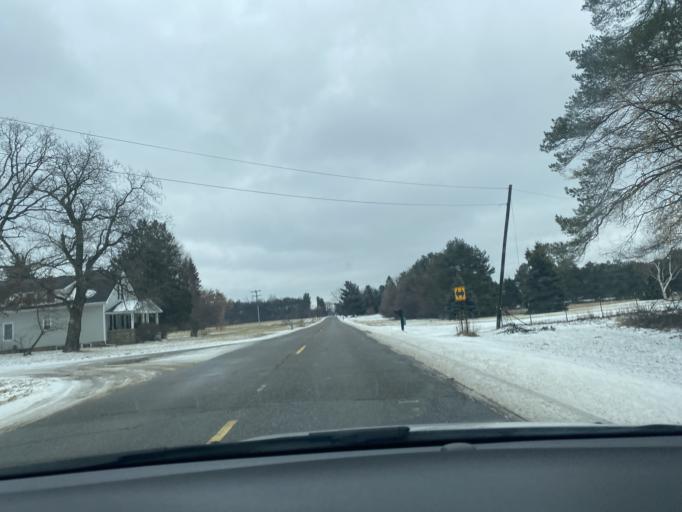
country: US
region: Michigan
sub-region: Lapeer County
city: Barnes Lake-Millers Lake
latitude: 43.2058
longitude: -83.2740
